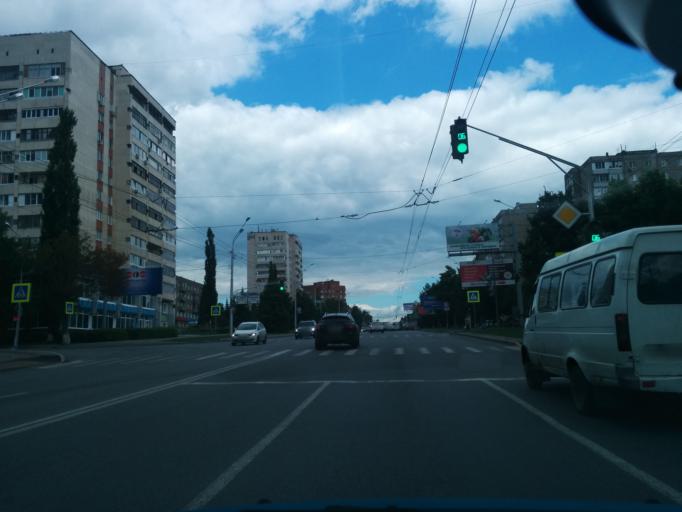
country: RU
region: Bashkortostan
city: Ufa
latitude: 54.7289
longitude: 55.9776
